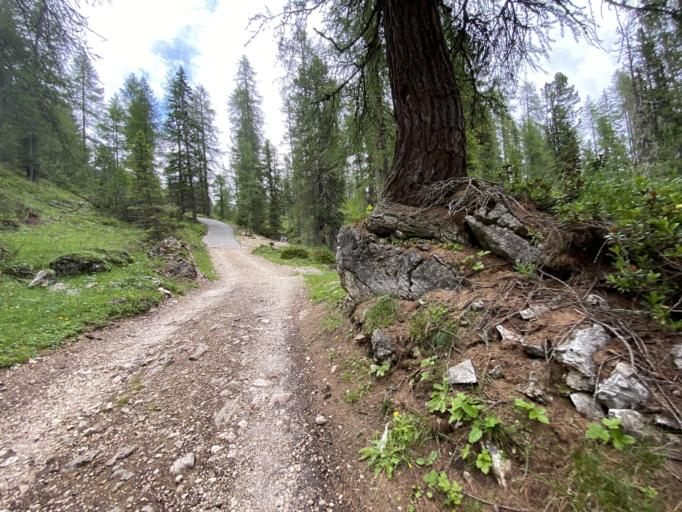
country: IT
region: Veneto
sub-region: Provincia di Belluno
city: Cortina d'Ampezzo
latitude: 46.4846
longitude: 12.1096
